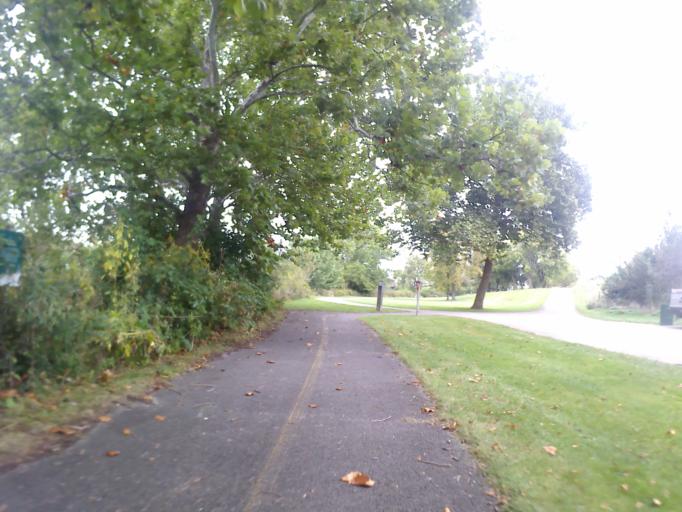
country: US
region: Illinois
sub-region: Kane County
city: Aurora
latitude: 41.7421
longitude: -88.3284
